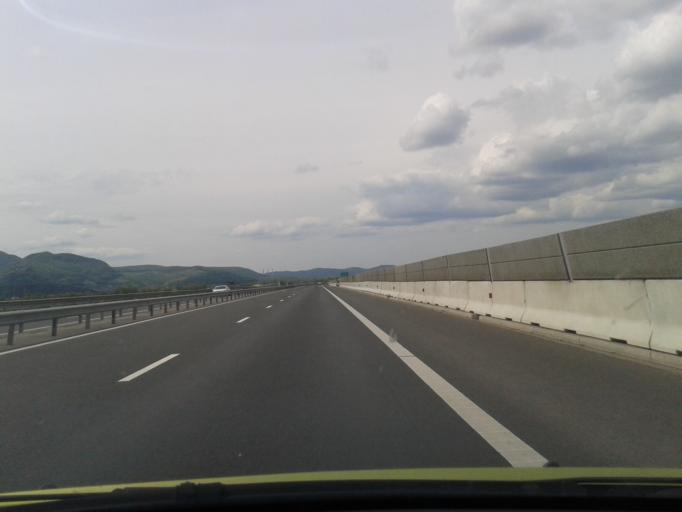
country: RO
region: Hunedoara
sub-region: Comuna Harau
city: Harau
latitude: 45.8923
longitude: 22.9540
